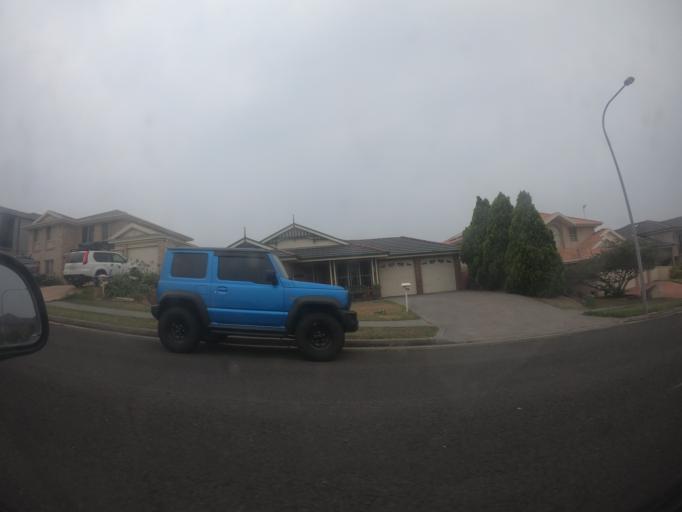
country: AU
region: New South Wales
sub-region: Shellharbour
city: Flinders
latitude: -34.5789
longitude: 150.8431
